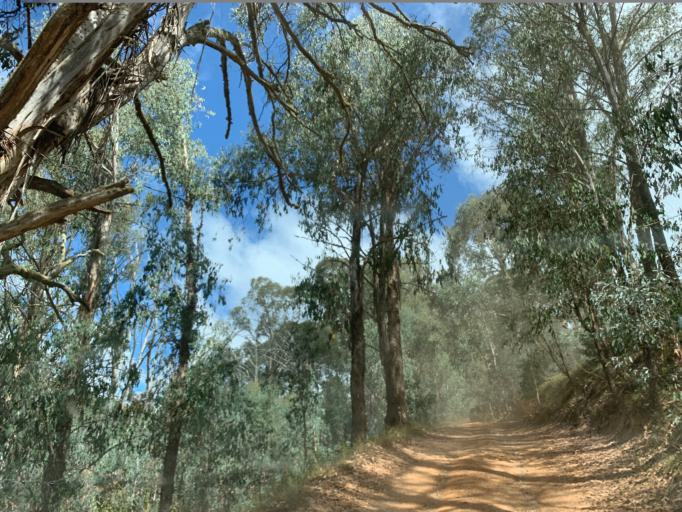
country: AU
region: Victoria
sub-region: Mansfield
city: Mansfield
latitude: -37.1072
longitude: 146.5358
